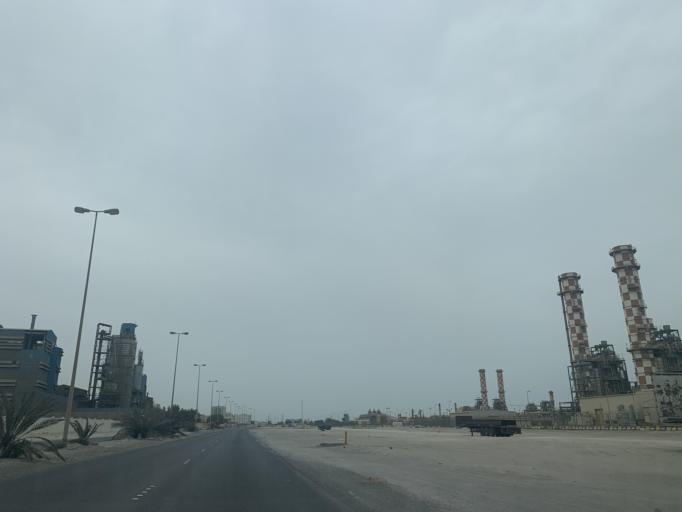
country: BH
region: Muharraq
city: Al Hadd
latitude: 26.2166
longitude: 50.6578
